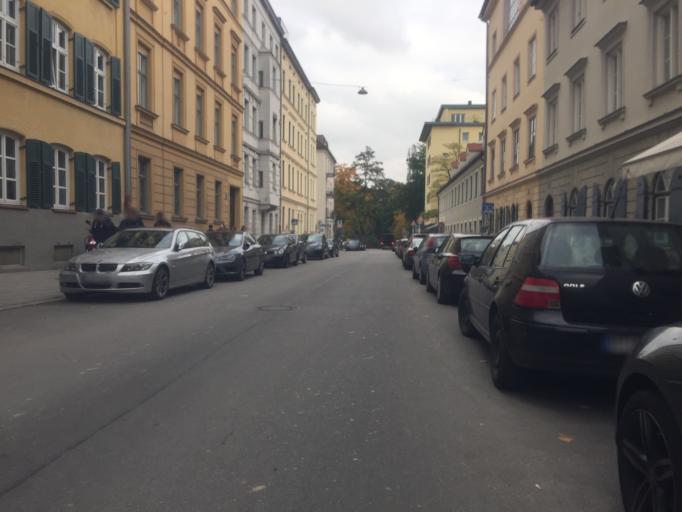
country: DE
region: Bavaria
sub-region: Upper Bavaria
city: Munich
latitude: 48.1503
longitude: 11.5830
